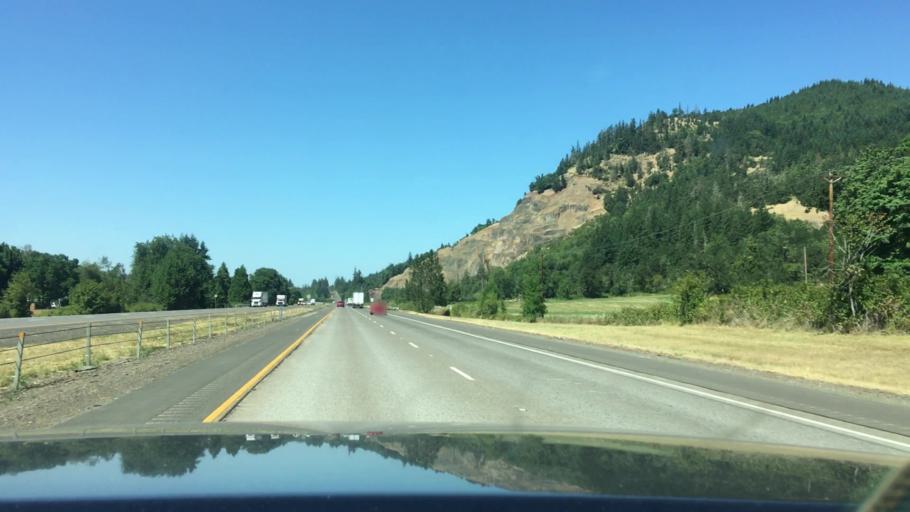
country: US
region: Oregon
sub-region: Lane County
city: Creswell
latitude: 43.8608
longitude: -123.0162
